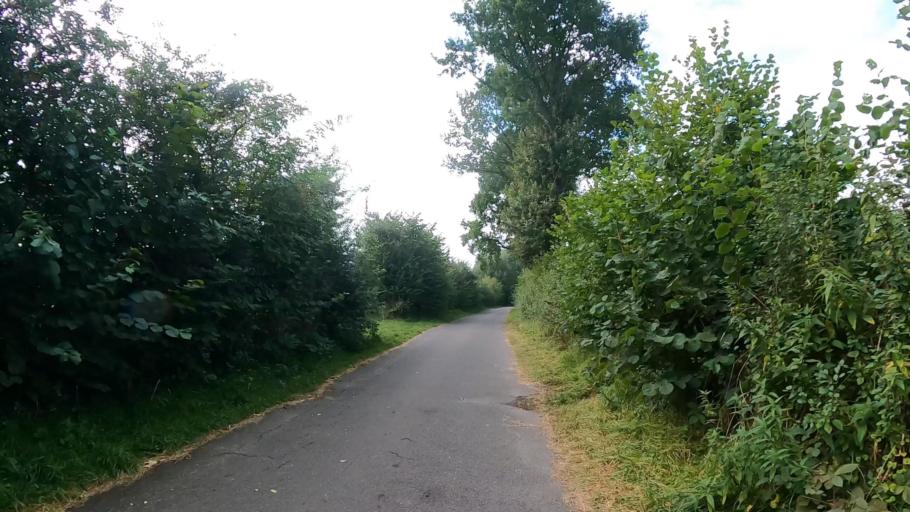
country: DE
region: Schleswig-Holstein
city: Kolln-Reisiek
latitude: 53.7320
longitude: 9.6821
